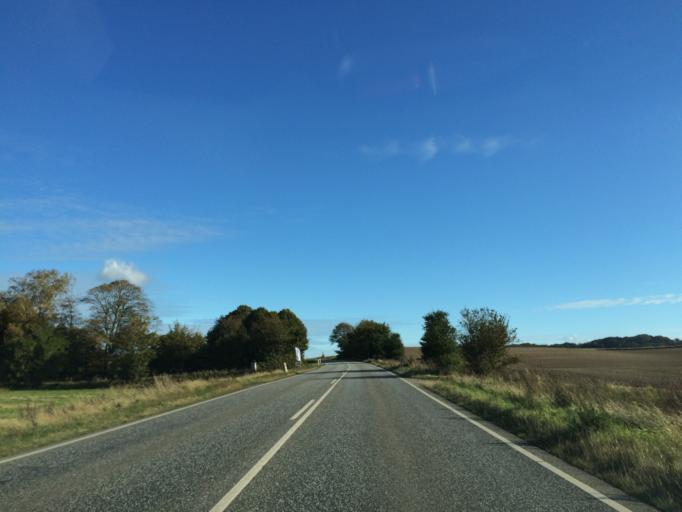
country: DK
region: Central Jutland
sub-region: Randers Kommune
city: Langa
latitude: 56.3788
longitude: 9.9515
